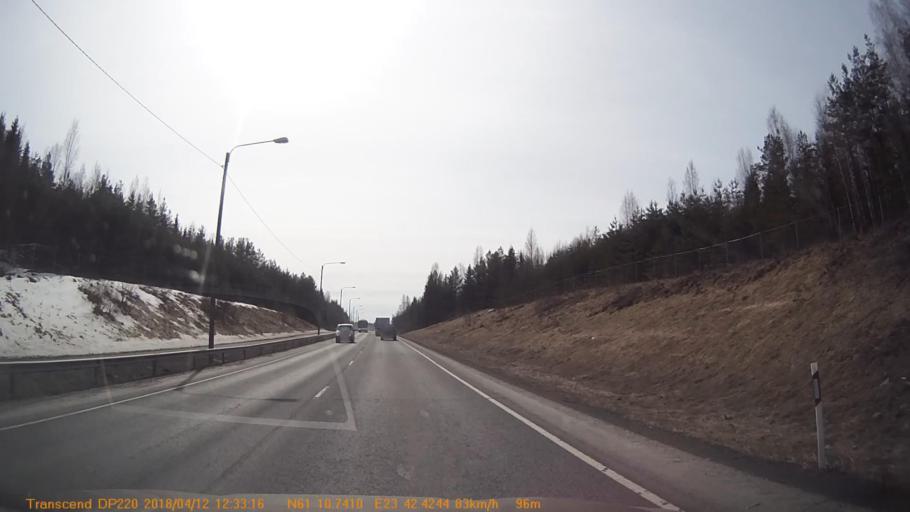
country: FI
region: Pirkanmaa
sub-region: Etelae-Pirkanmaa
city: Kylmaekoski
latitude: 61.1786
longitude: 23.7068
